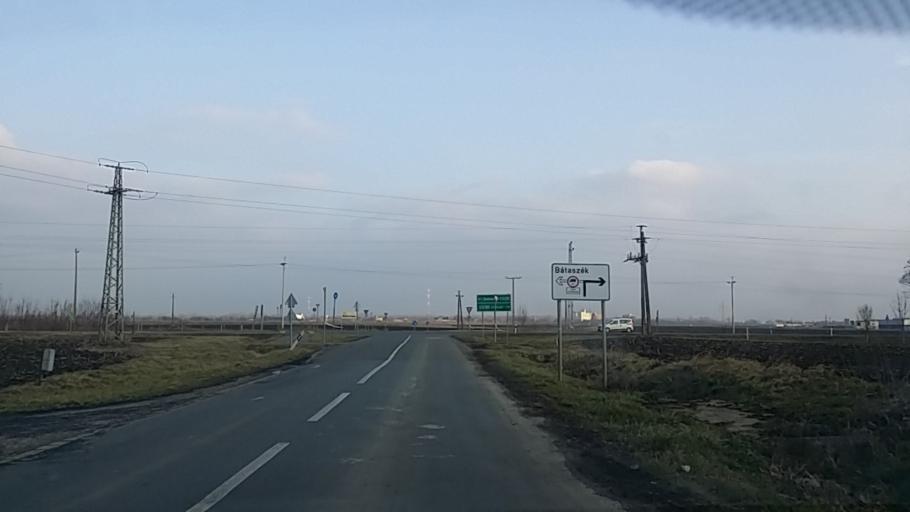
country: HU
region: Baranya
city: Lanycsok
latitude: 46.0174
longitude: 18.6557
